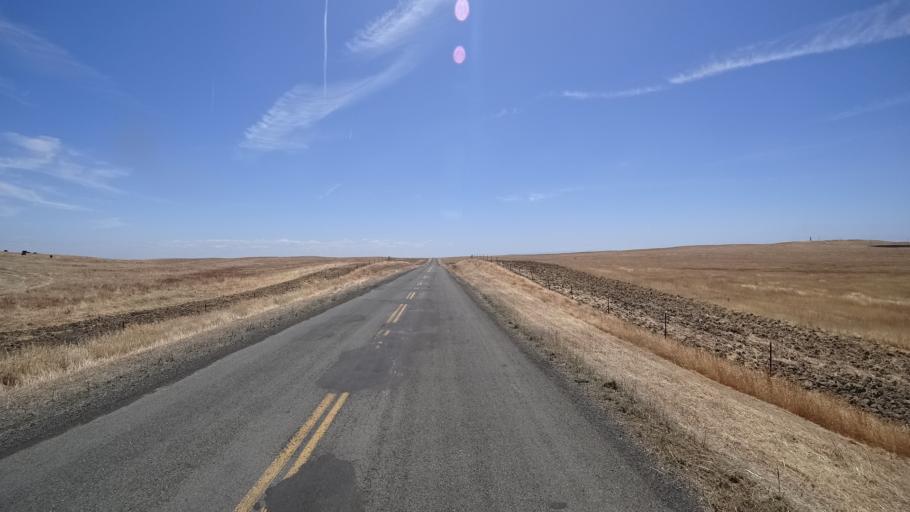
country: US
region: California
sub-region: Kings County
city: Kettleman City
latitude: 35.8262
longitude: -119.9103
